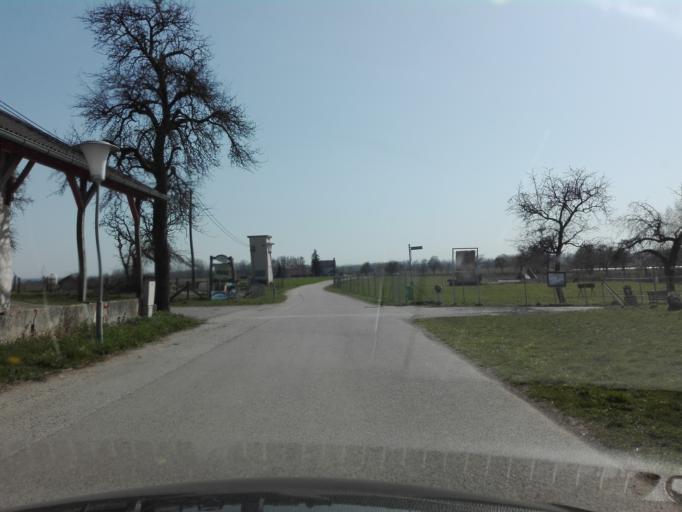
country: AT
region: Upper Austria
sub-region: Politischer Bezirk Perg
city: Perg
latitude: 48.2214
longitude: 14.6090
